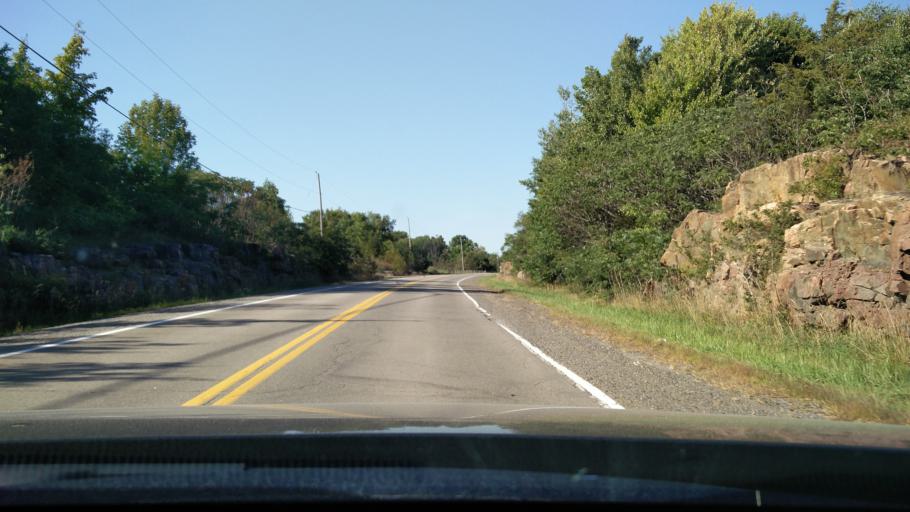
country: CA
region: Ontario
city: Perth
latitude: 44.6947
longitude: -76.4010
